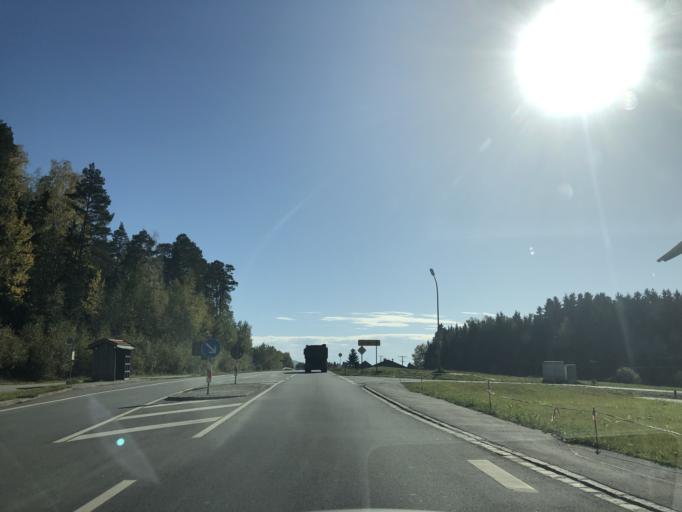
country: DE
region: Bavaria
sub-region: Lower Bavaria
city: Patersdorf
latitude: 49.0105
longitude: 12.9828
